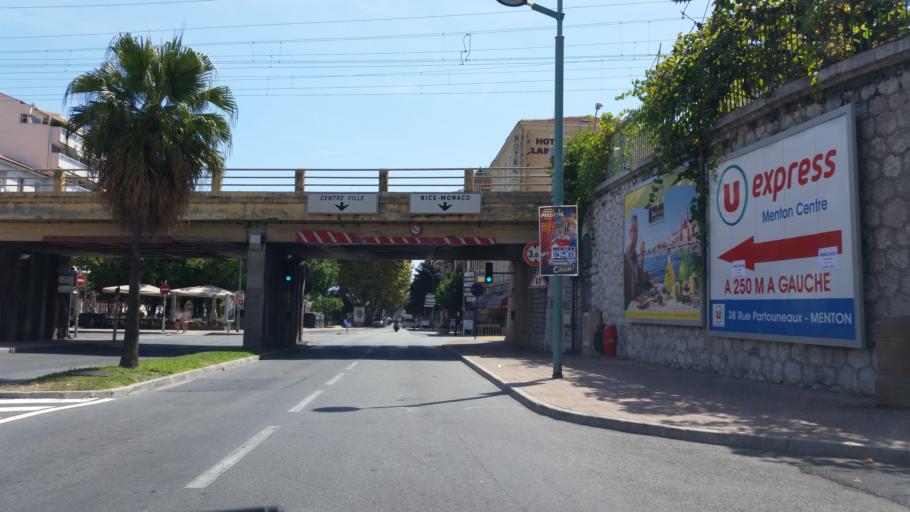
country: FR
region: Provence-Alpes-Cote d'Azur
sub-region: Departement des Alpes-Maritimes
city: Menton
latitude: 43.7759
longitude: 7.4946
